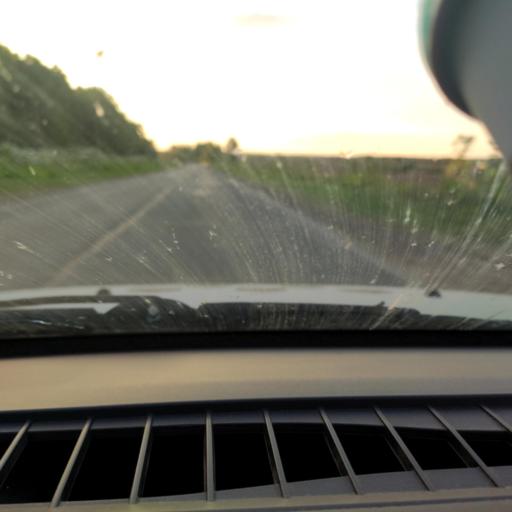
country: RU
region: Kirov
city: Kotel'nich
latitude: 58.5374
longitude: 48.2225
